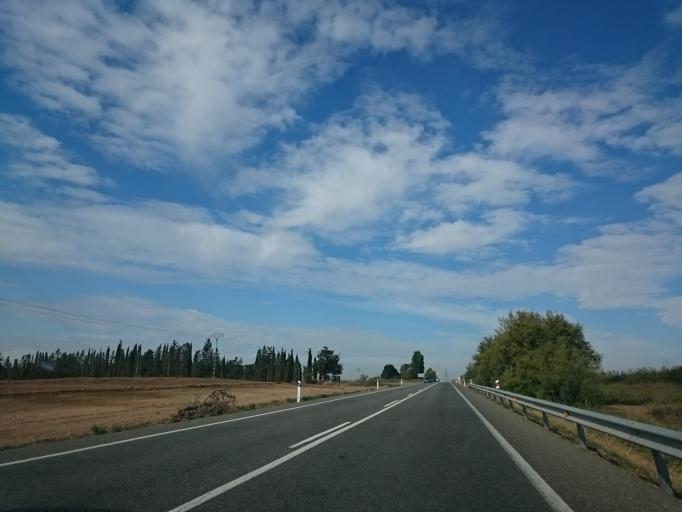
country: ES
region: Catalonia
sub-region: Provincia de Lleida
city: Alcoletge
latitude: 41.6022
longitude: 0.6871
